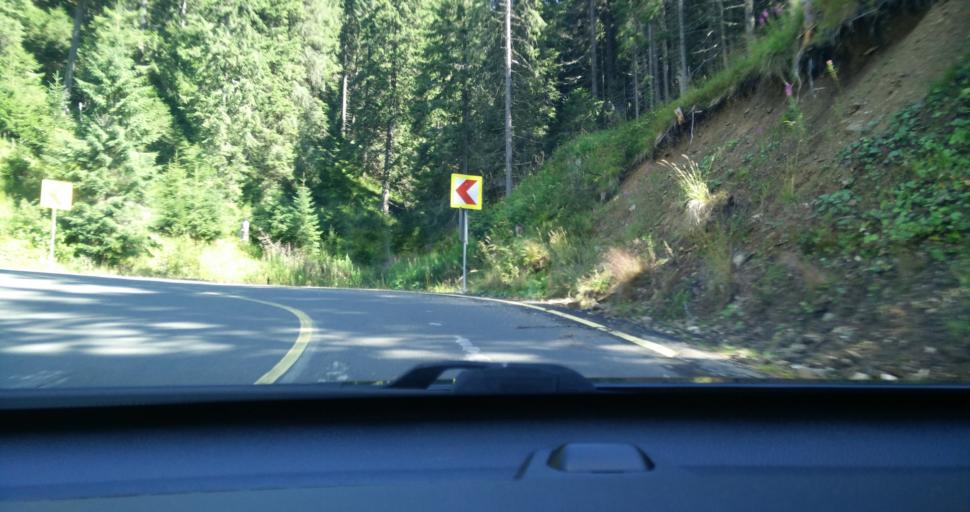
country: RO
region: Hunedoara
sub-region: Oras Petrila
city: Petrila
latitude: 45.4509
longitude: 23.6203
